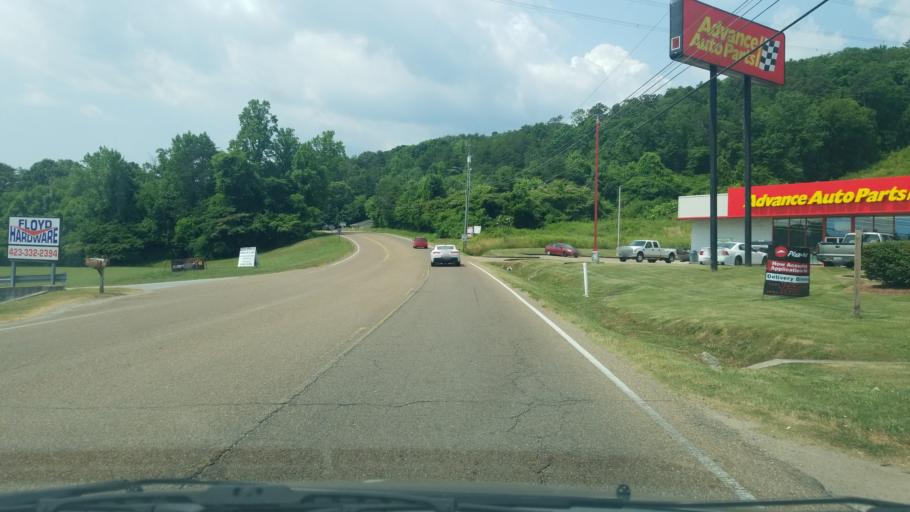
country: US
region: Tennessee
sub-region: Hamilton County
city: Soddy-Daisy
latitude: 35.2538
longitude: -85.1838
